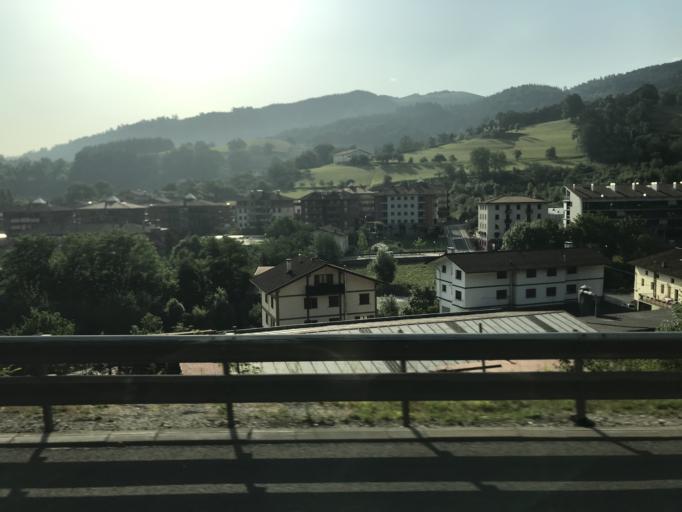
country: ES
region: Basque Country
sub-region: Provincia de Guipuzcoa
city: Idiazabal
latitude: 43.0089
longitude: -2.2365
